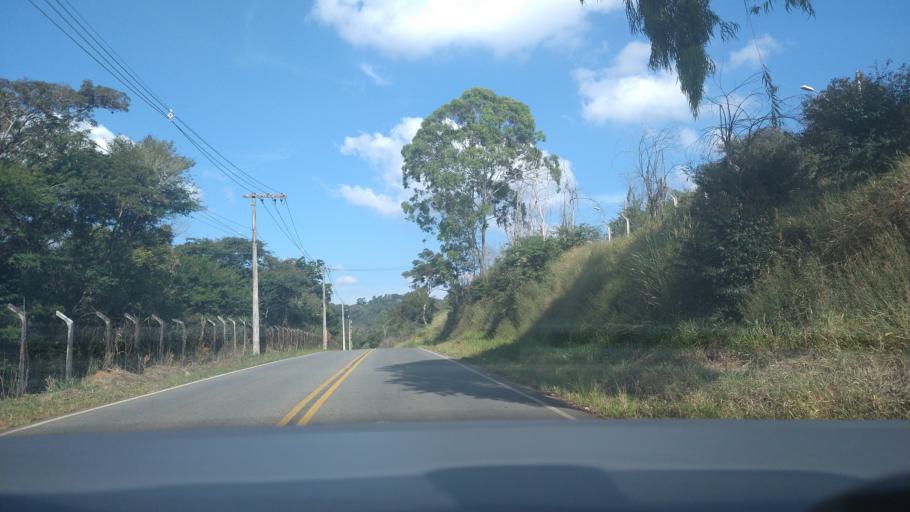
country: BR
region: Minas Gerais
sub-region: Vicosa
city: Vicosa
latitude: -20.7604
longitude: -42.8736
